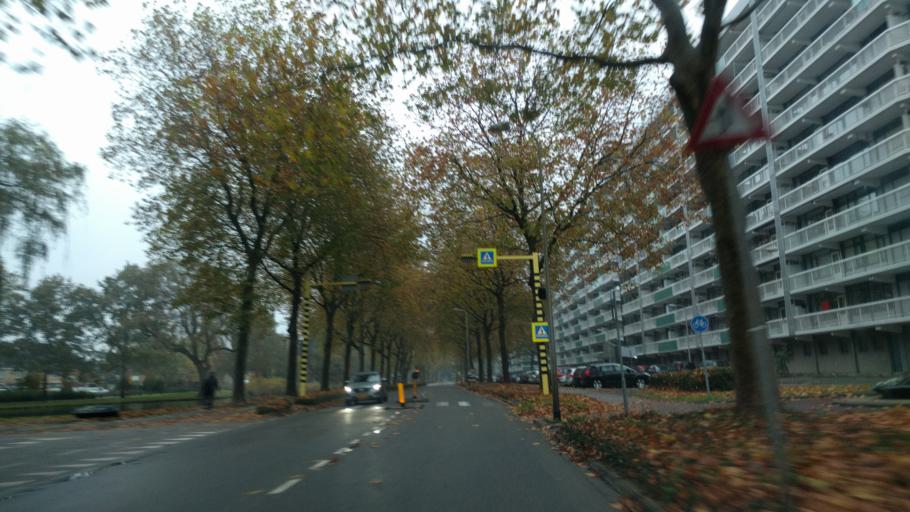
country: NL
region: South Holland
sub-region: Gemeente Ridderkerk
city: Ridderkerk
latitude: 51.8880
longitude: 4.5815
